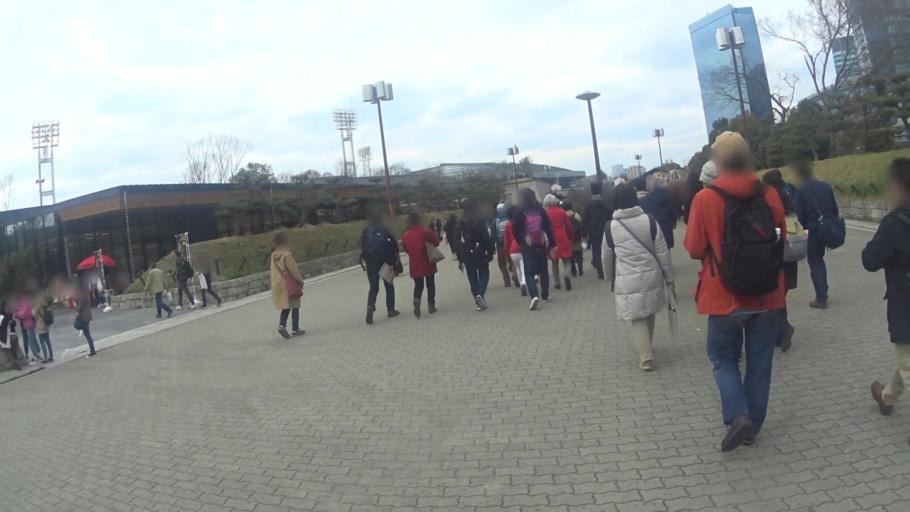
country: JP
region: Osaka
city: Osaka-shi
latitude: 34.6900
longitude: 135.5309
